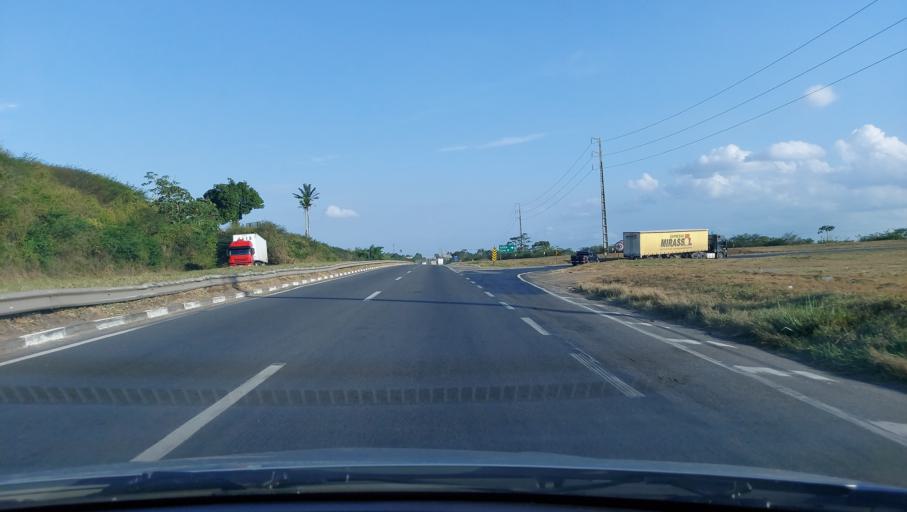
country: BR
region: Bahia
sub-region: Conceicao Do Jacuipe
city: Conceicao do Jacuipe
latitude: -12.3605
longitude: -38.8251
